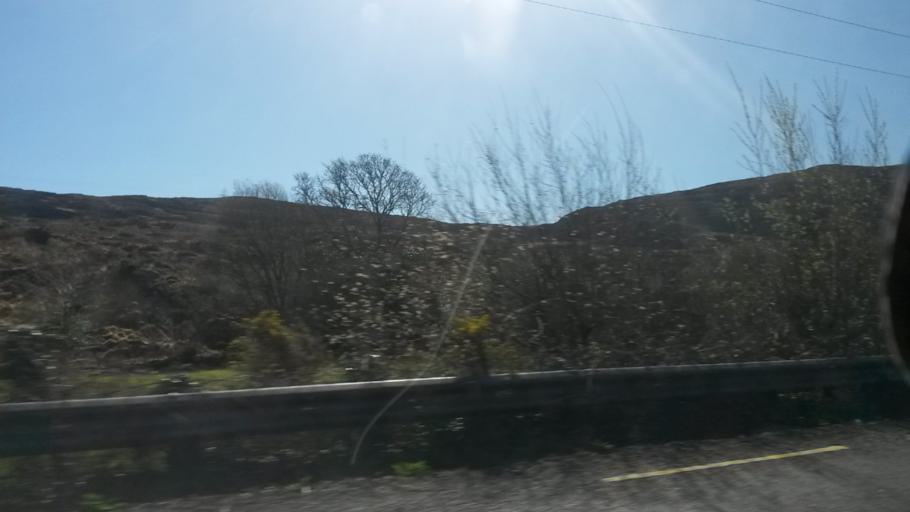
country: IE
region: Munster
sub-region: Ciarrai
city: Cill Airne
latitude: 51.9375
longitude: -9.3819
